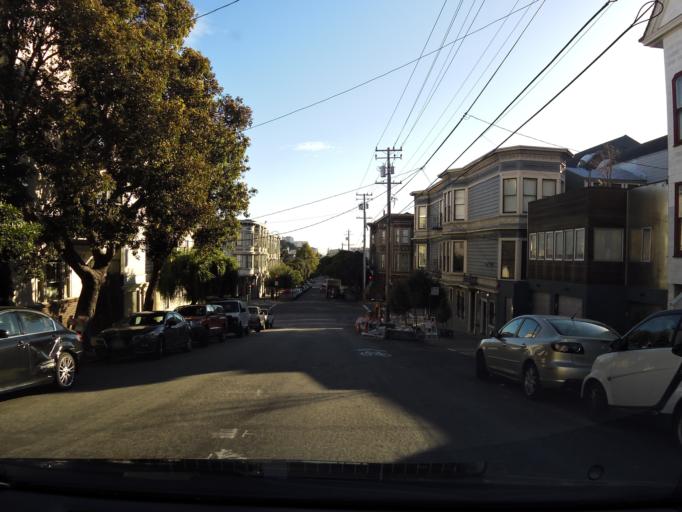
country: US
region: California
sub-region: San Francisco County
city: San Francisco
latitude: 37.7721
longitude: -122.4380
